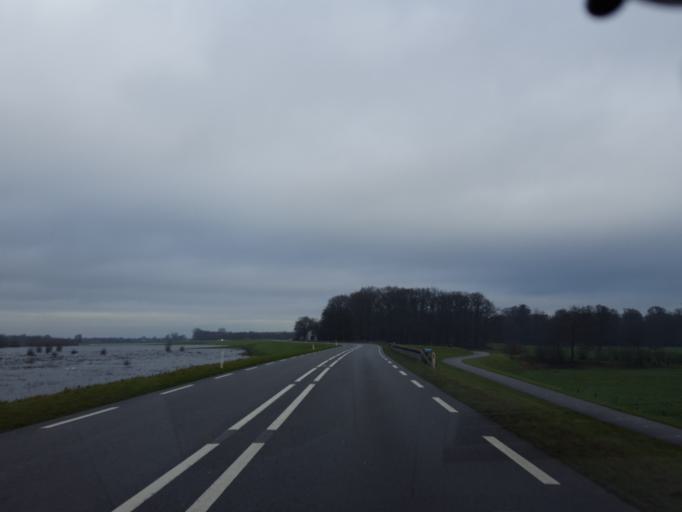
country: NL
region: Overijssel
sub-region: Gemeente Olst-Wijhe
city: Boskamp
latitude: 52.3019
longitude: 6.1115
